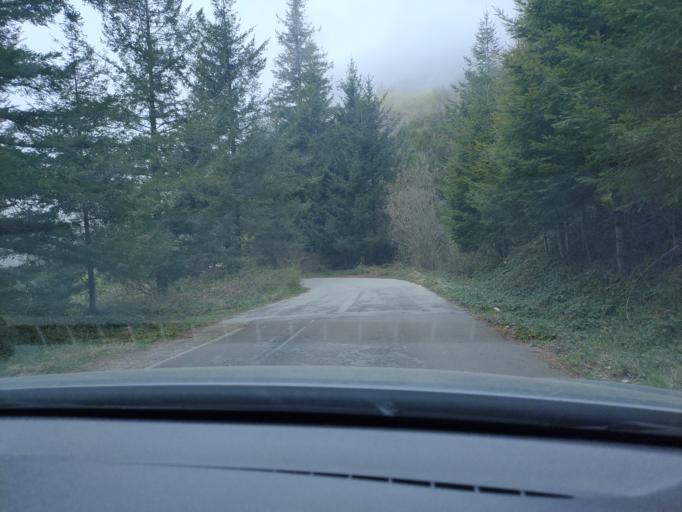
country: ES
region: Catalonia
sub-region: Provincia de Barcelona
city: Fogars de Montclus
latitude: 41.7566
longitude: 2.4560
